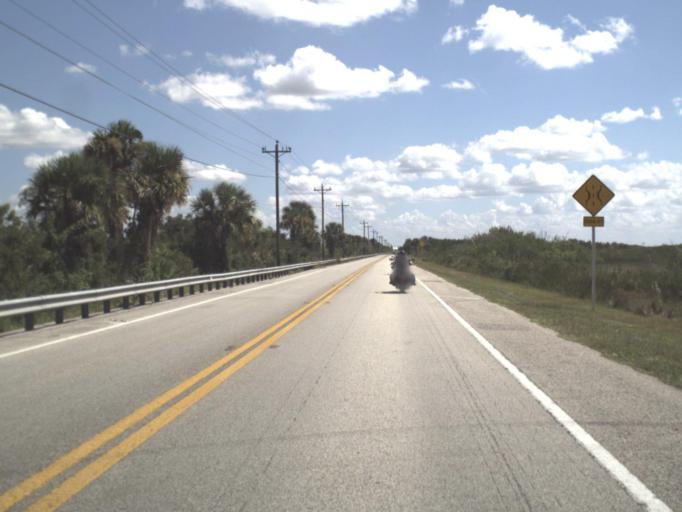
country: US
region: Florida
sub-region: Collier County
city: Marco
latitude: 25.9555
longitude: -81.4881
